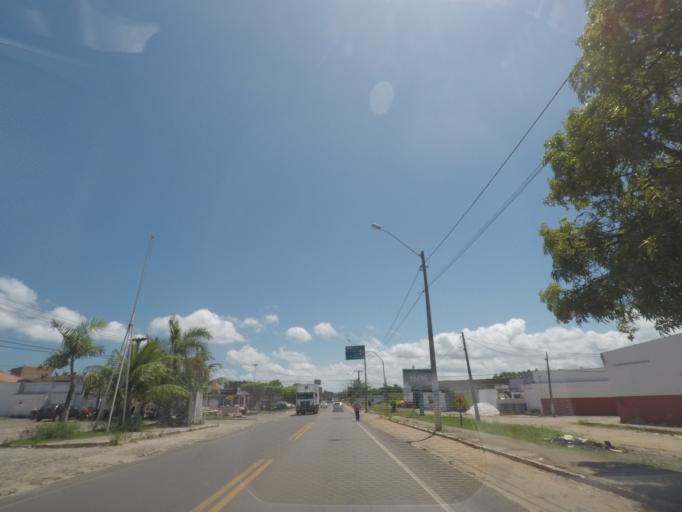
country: BR
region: Bahia
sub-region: Valenca
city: Valenca
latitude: -13.3504
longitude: -39.0610
